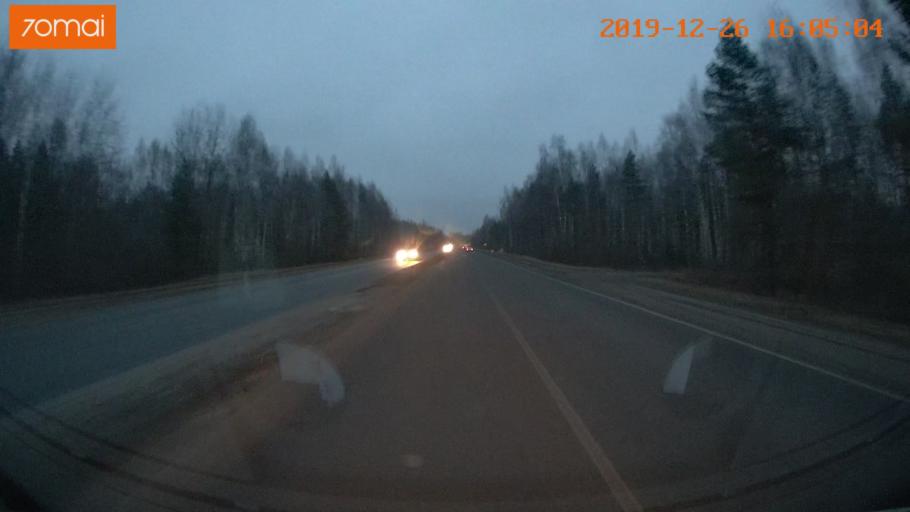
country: RU
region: Jaroslavl
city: Rybinsk
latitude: 58.0073
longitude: 38.8861
